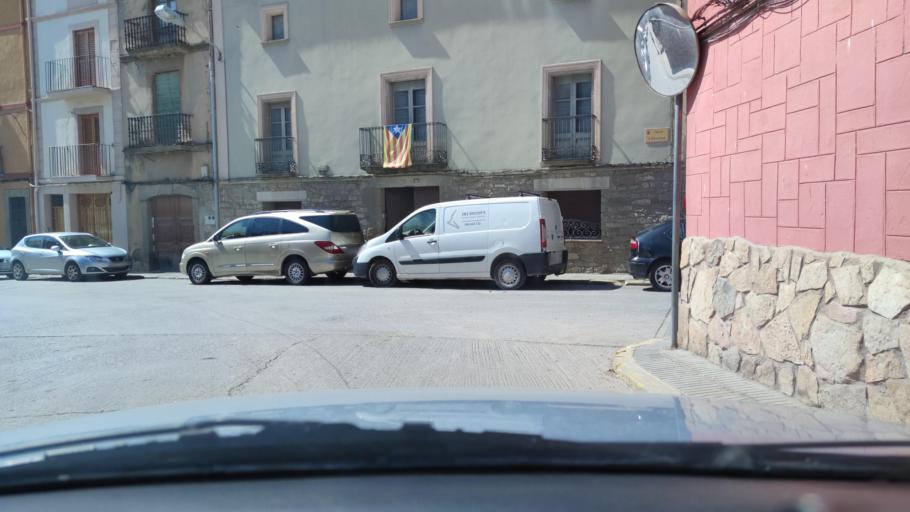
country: ES
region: Catalonia
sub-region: Provincia de Lleida
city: Castellsera
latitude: 41.7465
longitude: 0.9859
